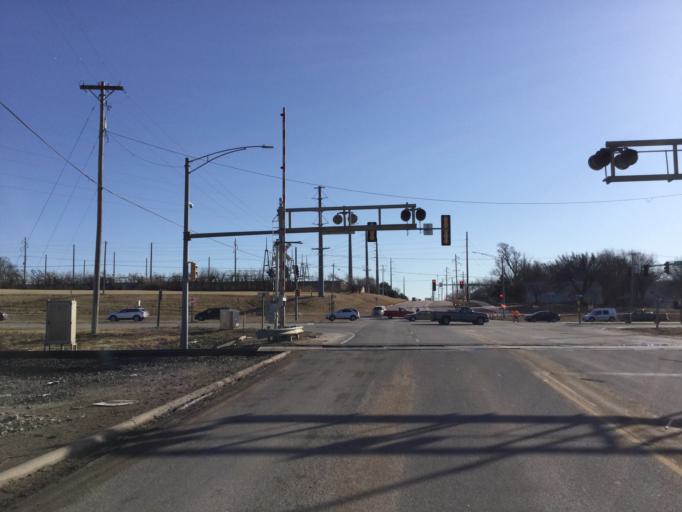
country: US
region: Kansas
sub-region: Sedgwick County
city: Derby
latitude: 37.6059
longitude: -97.2917
